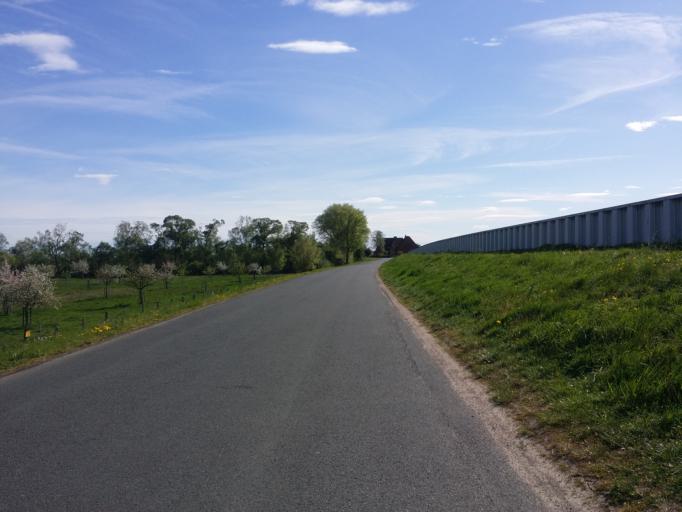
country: DE
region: Lower Saxony
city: Lemwerder
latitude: 53.1582
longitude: 8.6316
